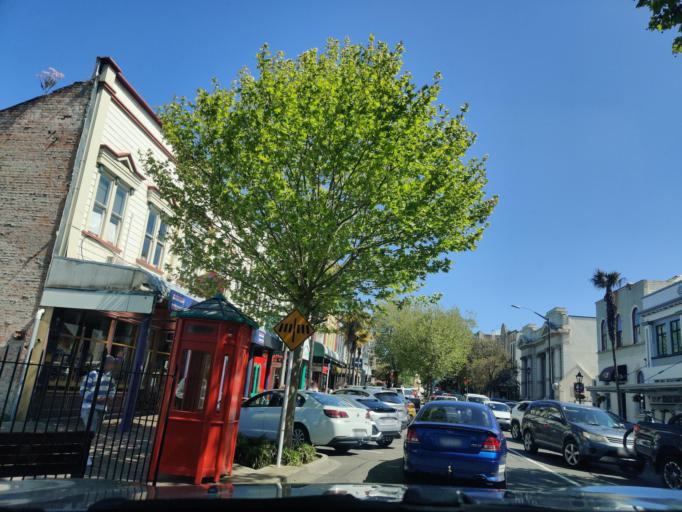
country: NZ
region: Manawatu-Wanganui
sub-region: Wanganui District
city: Wanganui
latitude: -39.9349
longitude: 175.0552
